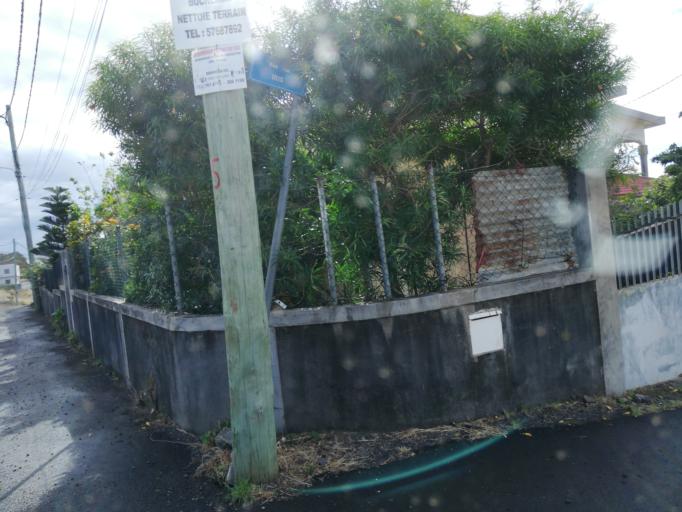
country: MU
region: Black River
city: Petite Riviere
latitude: -20.2034
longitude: 57.4645
